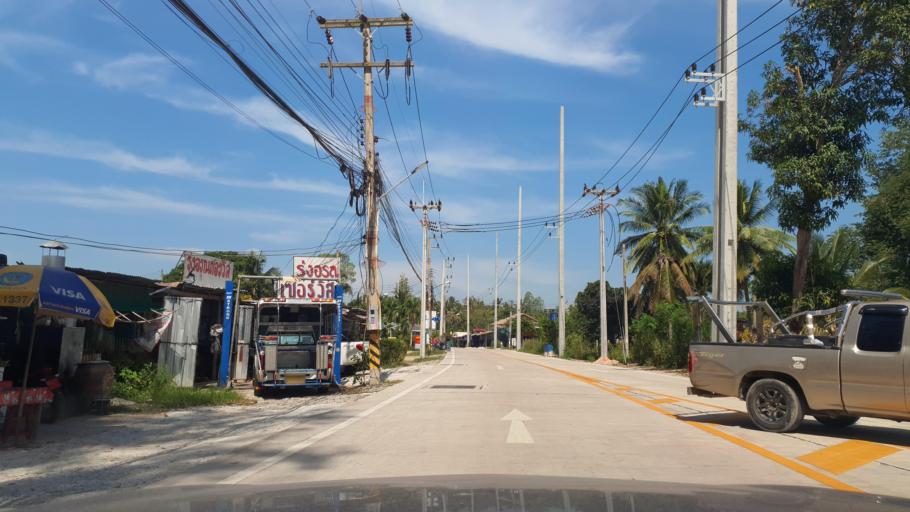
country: TH
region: Chon Buri
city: Bang Lamung
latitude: 12.9834
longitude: 100.9644
